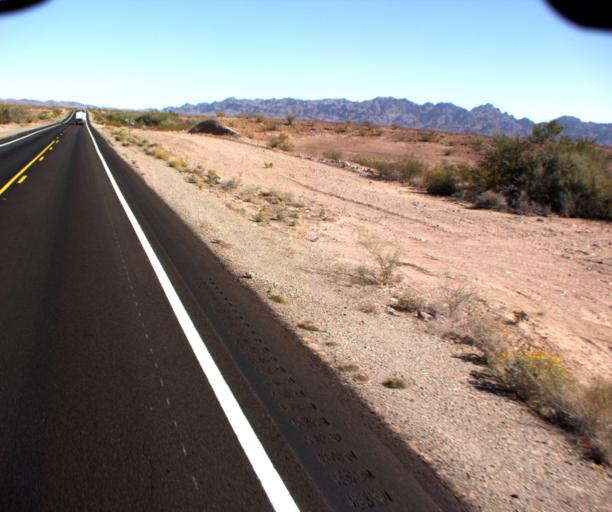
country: US
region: Arizona
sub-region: Yuma County
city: Wellton
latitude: 33.1200
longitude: -114.2923
